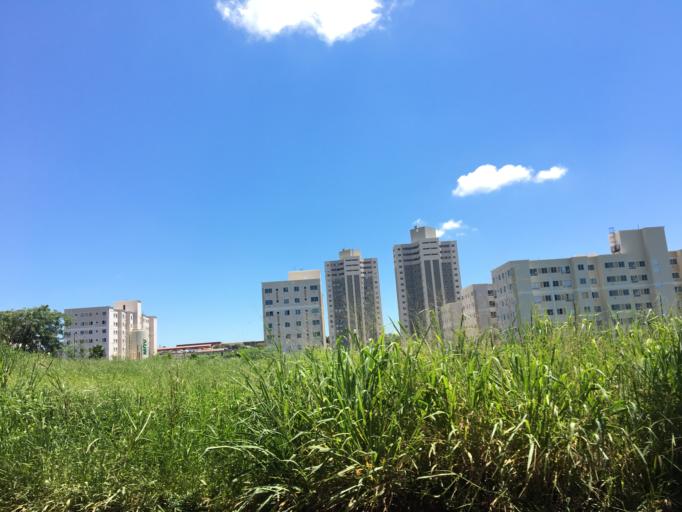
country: BR
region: Parana
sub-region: Maringa
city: Maringa
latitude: -23.4475
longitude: -51.9798
